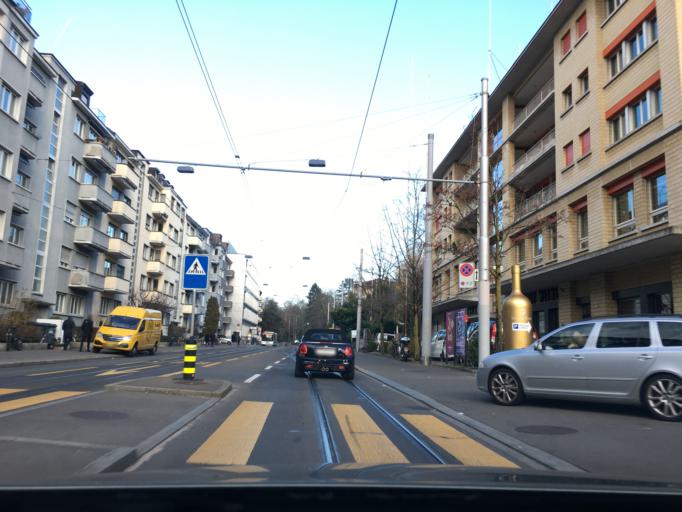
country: CH
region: Zurich
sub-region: Bezirk Zuerich
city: Zuerich (Kreis 2) / Enge
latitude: 47.3625
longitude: 8.5270
